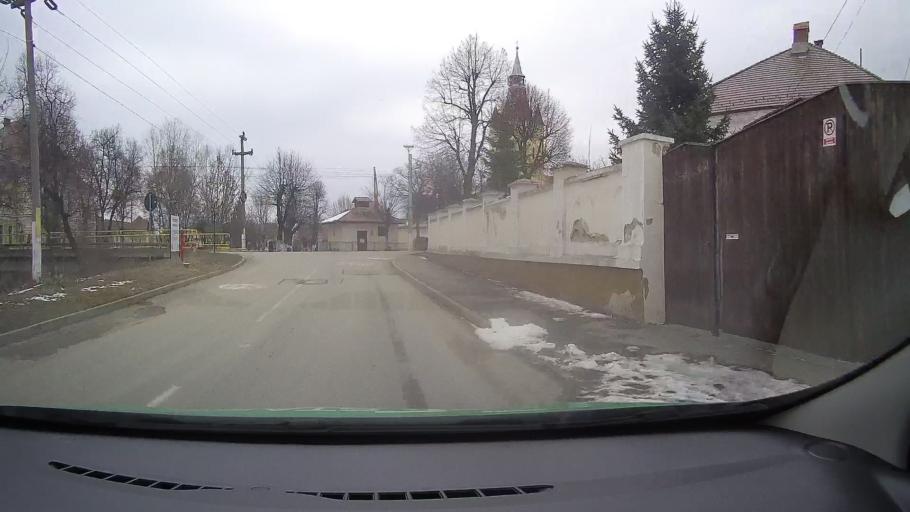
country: RO
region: Brasov
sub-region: Comuna Cristian
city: Cristian
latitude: 45.6247
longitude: 25.4792
